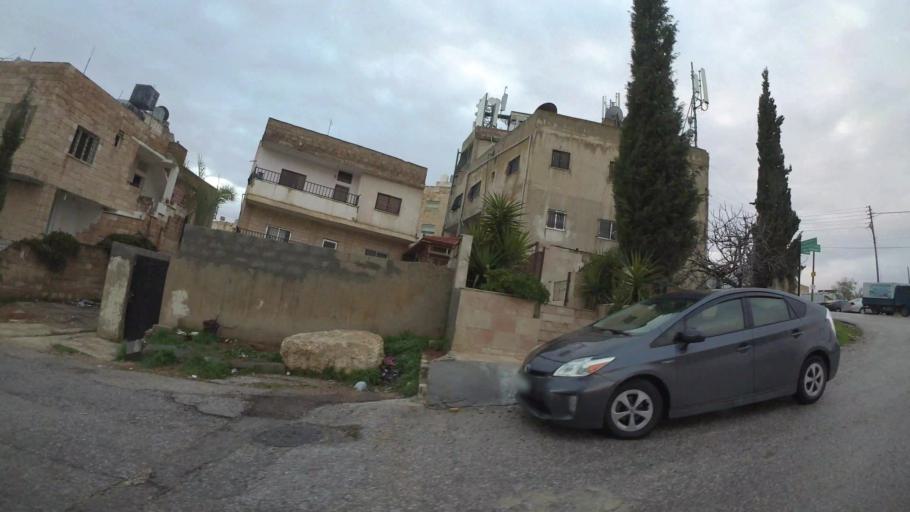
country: JO
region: Amman
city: Amman
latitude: 31.9834
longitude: 35.9140
